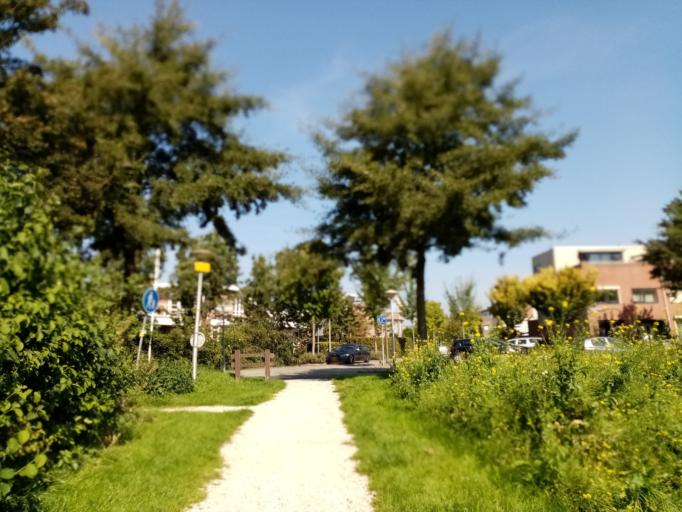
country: NL
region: South Holland
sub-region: Gemeente Lisse
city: Lisse
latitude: 52.2402
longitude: 4.5595
